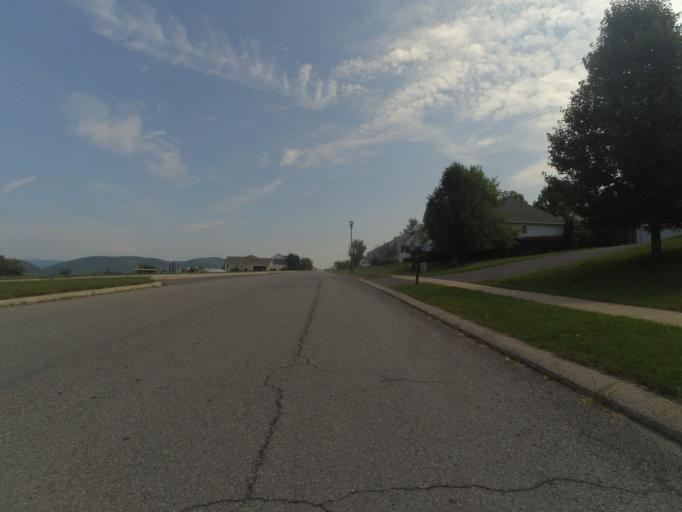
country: US
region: Pennsylvania
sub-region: Centre County
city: Bellefonte
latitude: 40.8976
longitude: -77.7839
